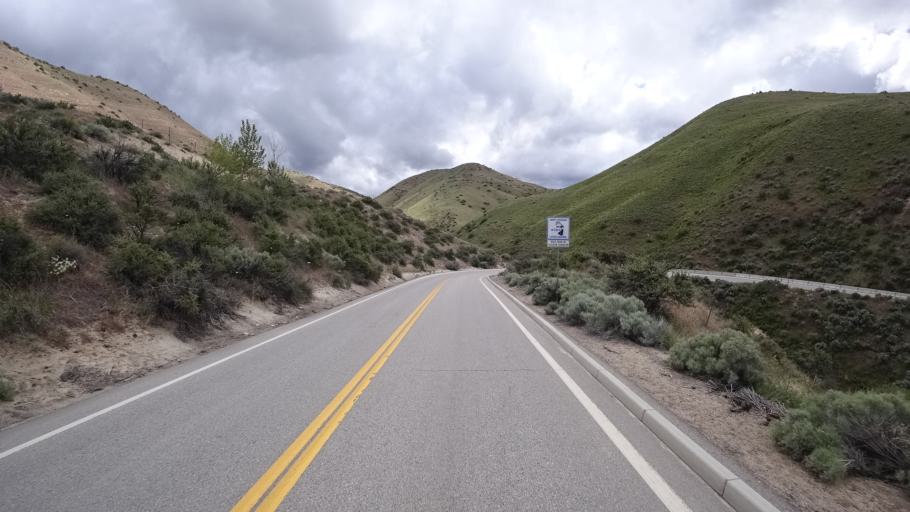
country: US
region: Idaho
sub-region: Ada County
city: Boise
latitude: 43.6825
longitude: -116.1804
